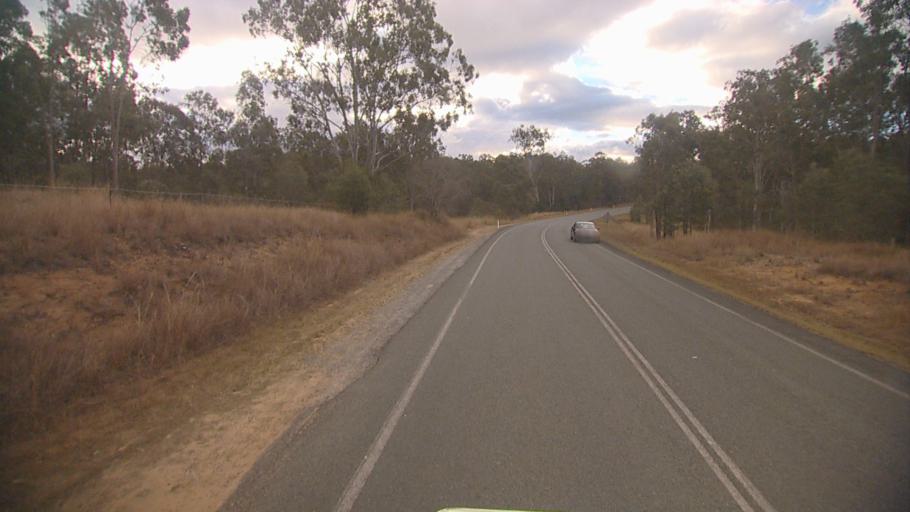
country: AU
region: Queensland
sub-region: Logan
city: Cedar Vale
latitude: -27.9098
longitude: 153.0904
